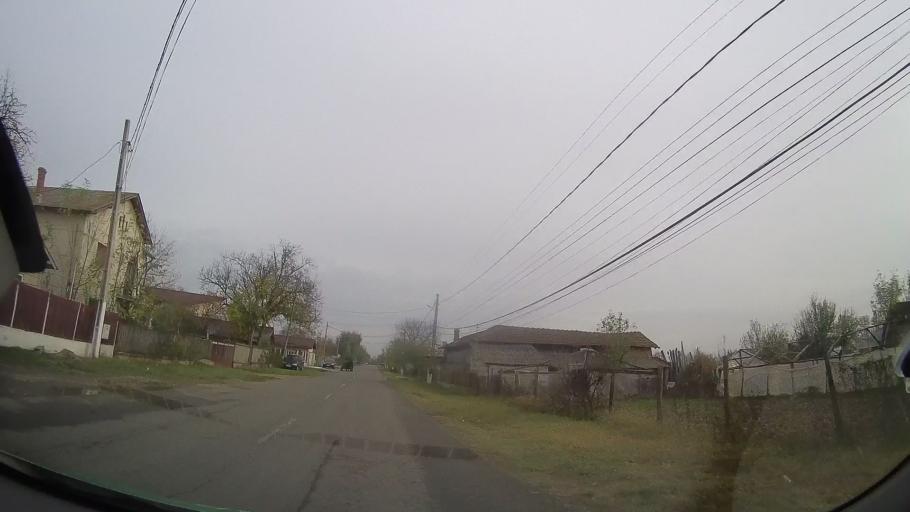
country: RO
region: Prahova
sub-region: Comuna Balta Doamnei
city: Balta Doamnei
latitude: 44.7604
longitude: 26.1601
